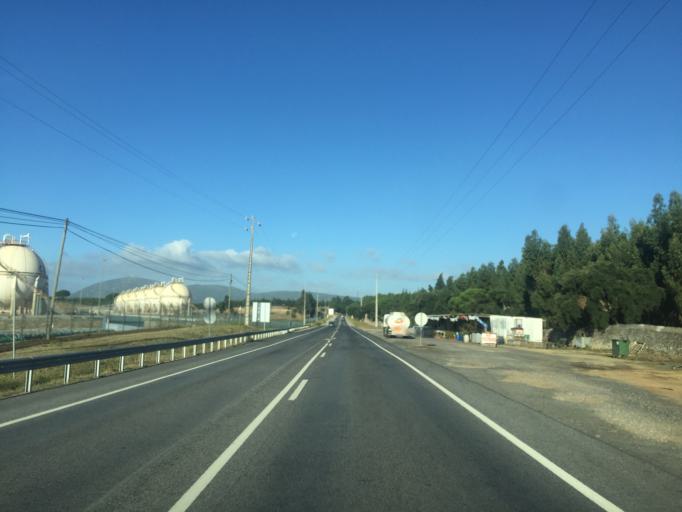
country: PT
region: Lisbon
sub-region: Azambuja
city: Aveiras de Cima
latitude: 39.1717
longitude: -8.9271
